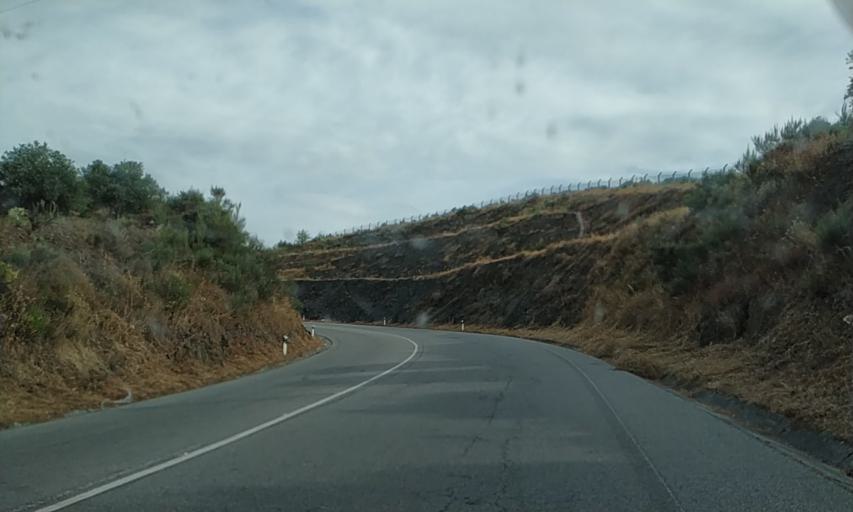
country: PT
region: Viseu
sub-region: Sao Joao da Pesqueira
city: Sao Joao da Pesqueira
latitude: 41.1292
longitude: -7.3981
